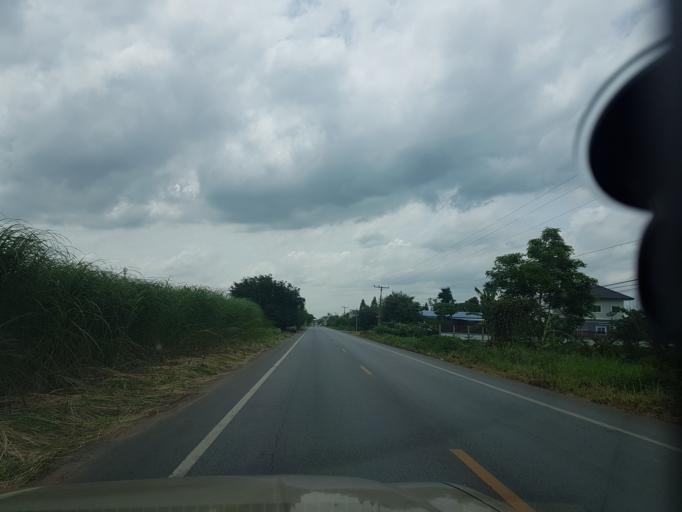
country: TH
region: Sara Buri
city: Nong Khae
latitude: 14.2707
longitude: 100.8918
